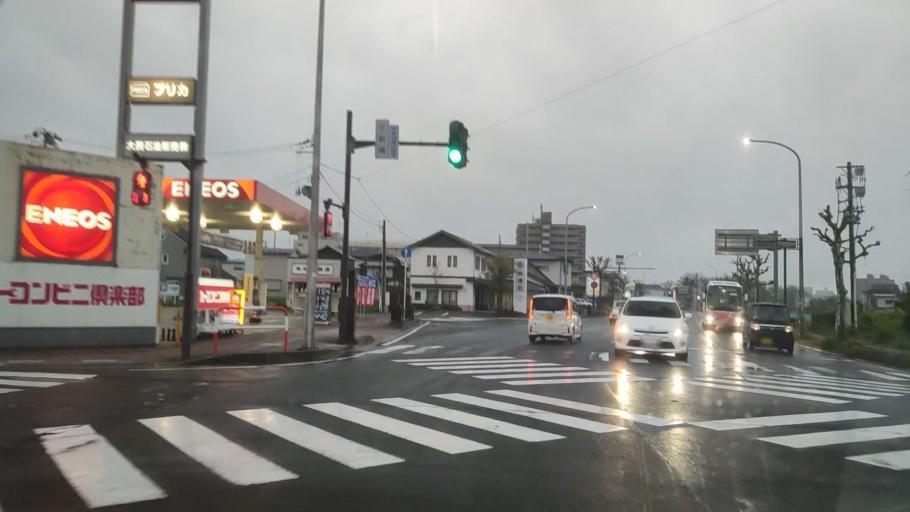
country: JP
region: Akita
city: Akita
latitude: 39.7102
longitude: 140.1159
